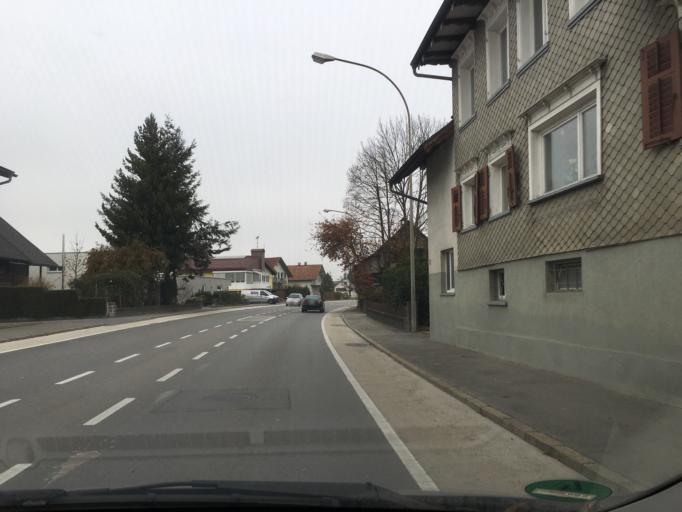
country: AT
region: Vorarlberg
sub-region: Politischer Bezirk Dornbirn
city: Hohenems
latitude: 47.3610
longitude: 9.6665
